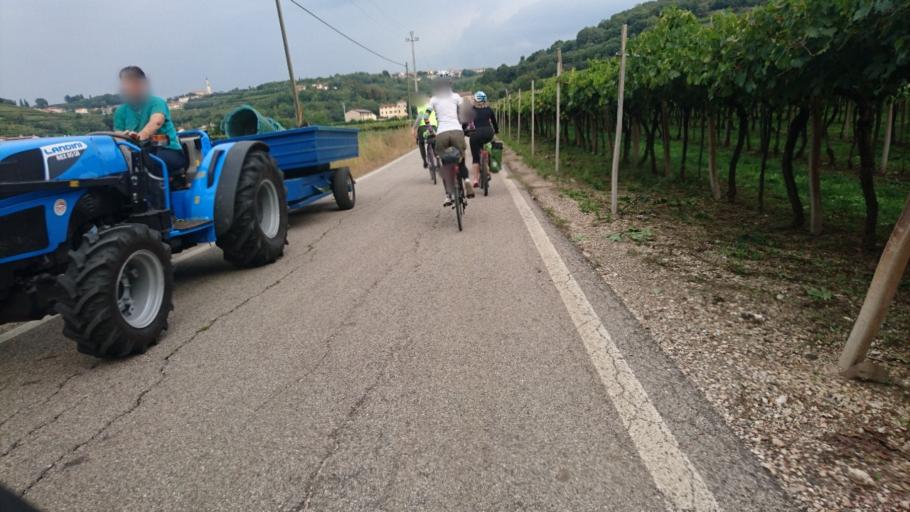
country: IT
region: Veneto
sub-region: Provincia di Verona
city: Colognola ai Colli
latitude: 45.4197
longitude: 11.1969
